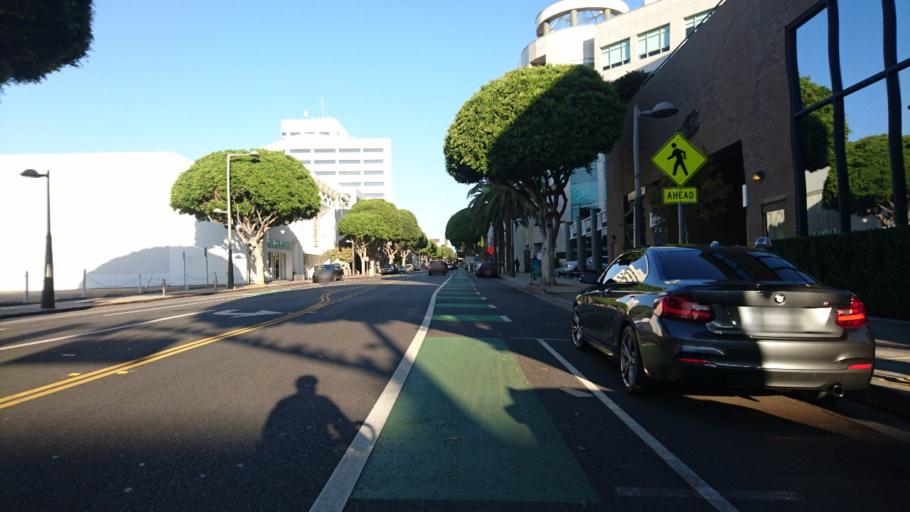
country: US
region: California
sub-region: Los Angeles County
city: Santa Monica
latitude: 34.0151
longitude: -118.4972
